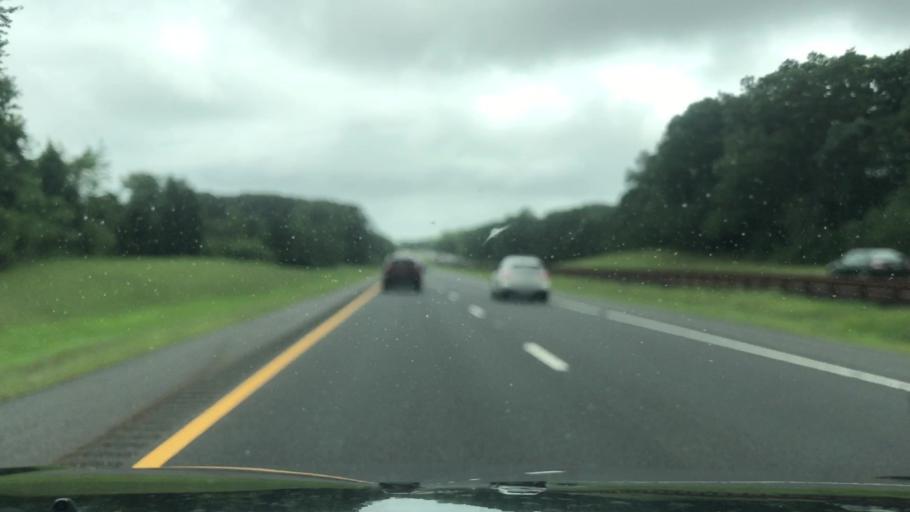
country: US
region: New Jersey
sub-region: Monmouth County
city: Eatontown
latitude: 40.2651
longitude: -74.0792
